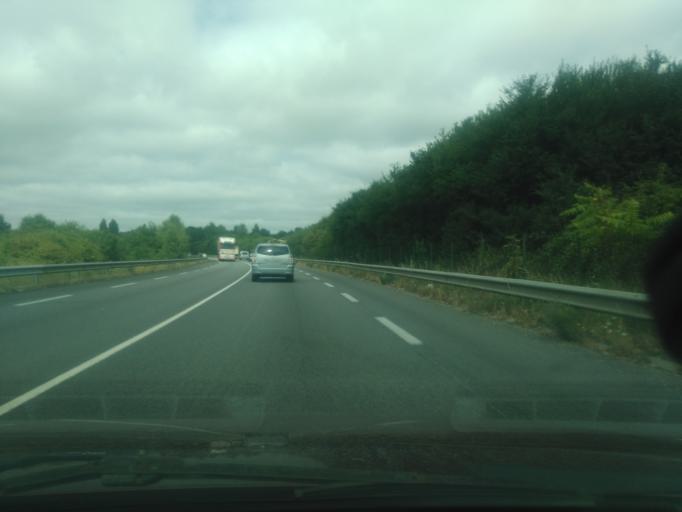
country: FR
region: Pays de la Loire
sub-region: Departement de la Vendee
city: La Roche-sur-Yon
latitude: 46.6910
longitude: -1.4166
